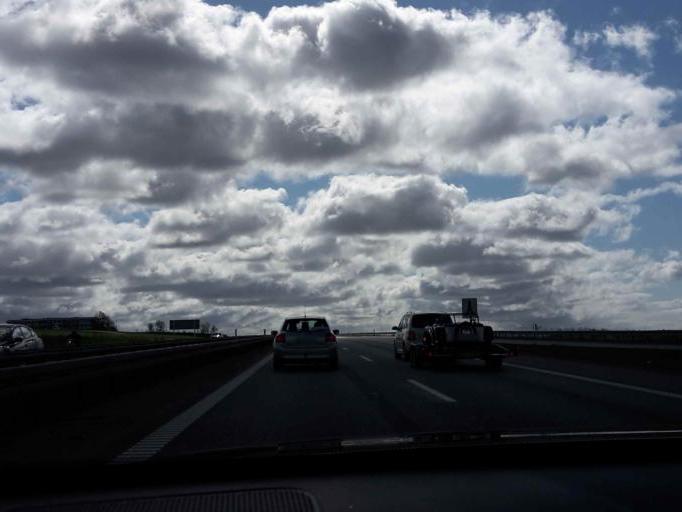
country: DK
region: Central Jutland
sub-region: Arhus Kommune
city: Trige
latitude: 56.2184
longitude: 10.1346
